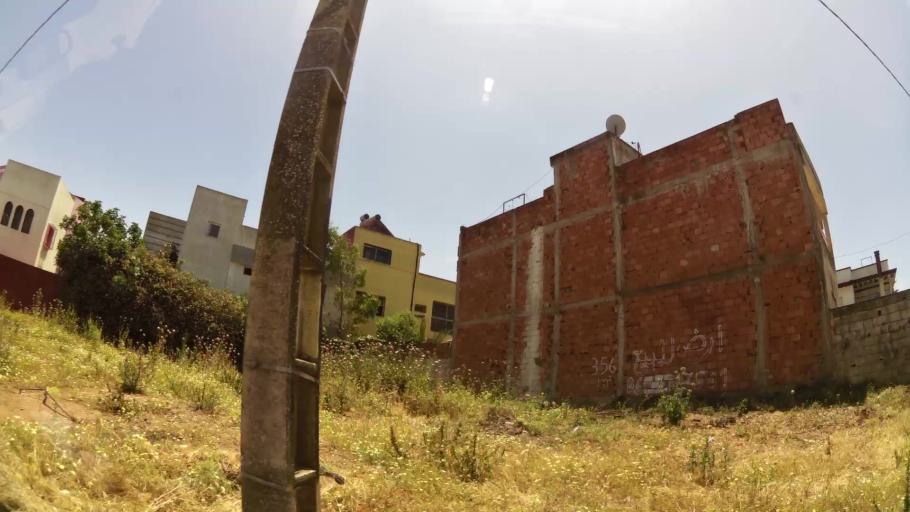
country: MA
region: Gharb-Chrarda-Beni Hssen
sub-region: Kenitra Province
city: Kenitra
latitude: 34.2647
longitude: -6.6214
